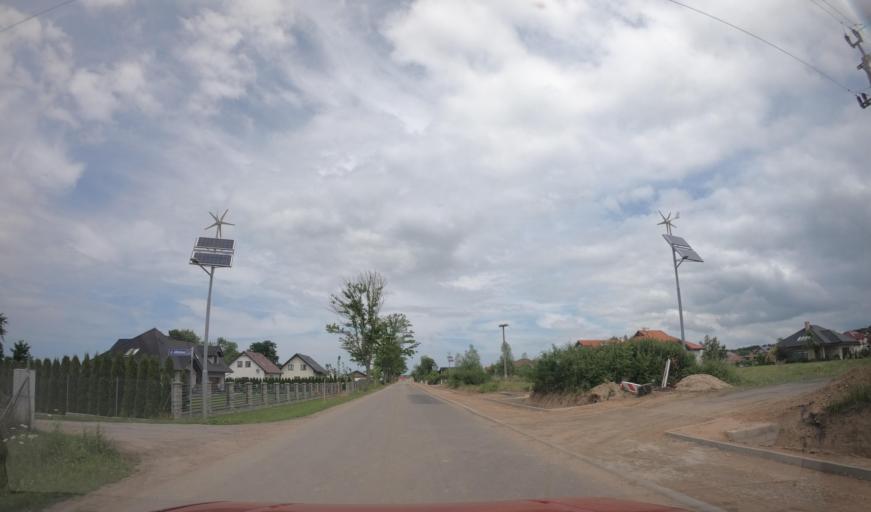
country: PL
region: West Pomeranian Voivodeship
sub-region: Powiat koszalinski
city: Mielno
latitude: 54.2228
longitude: 16.1027
